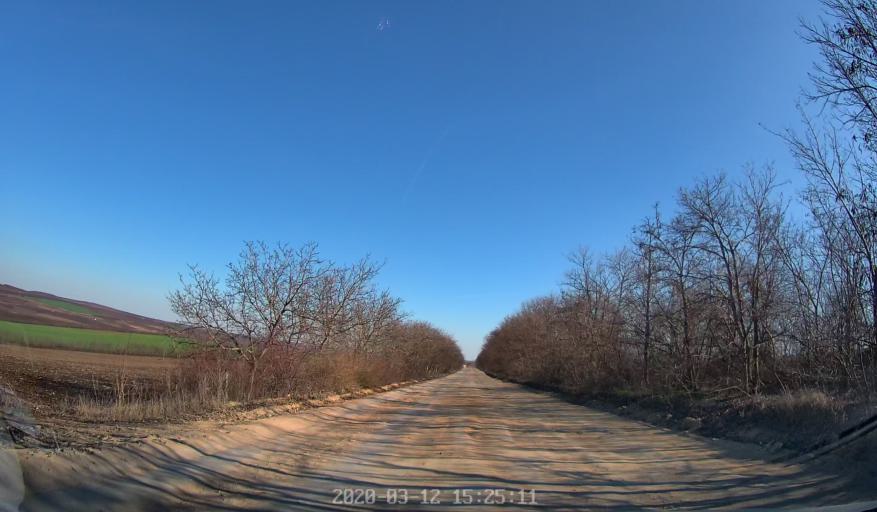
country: MD
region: Chisinau
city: Ciorescu
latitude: 47.1836
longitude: 28.9172
